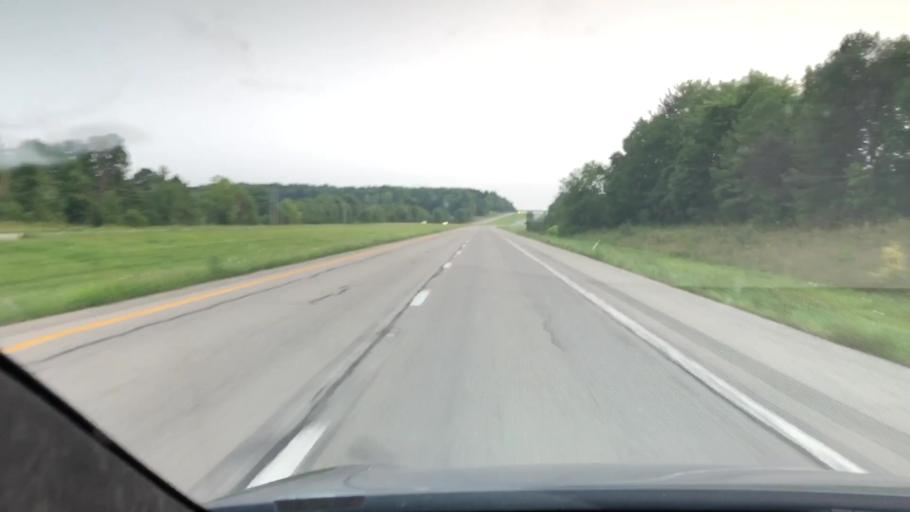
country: US
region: Pennsylvania
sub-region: Venango County
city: Sugarcreek
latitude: 41.2607
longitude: -79.9305
